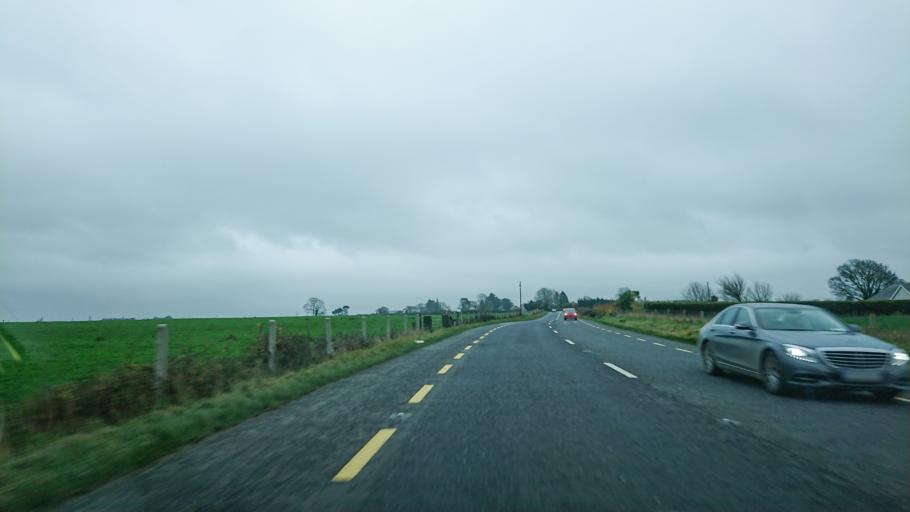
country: IE
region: Leinster
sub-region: Kilkenny
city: Mooncoin
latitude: 52.2844
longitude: -7.2118
